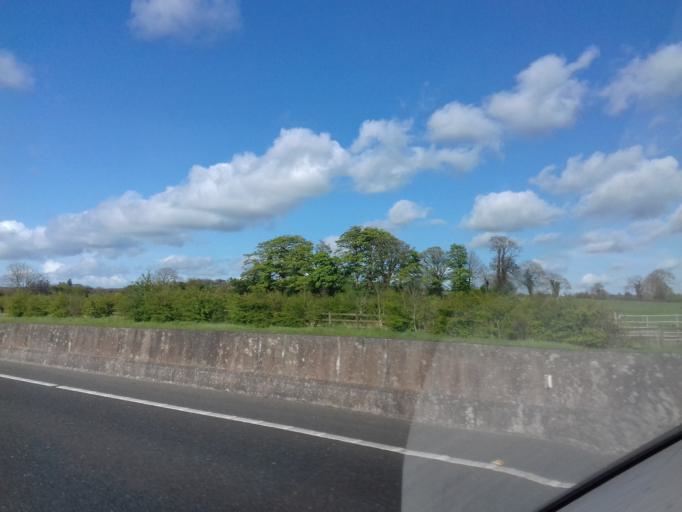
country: IE
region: Leinster
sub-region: Kilkenny
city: Mooncoin
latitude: 52.3614
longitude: -7.1653
